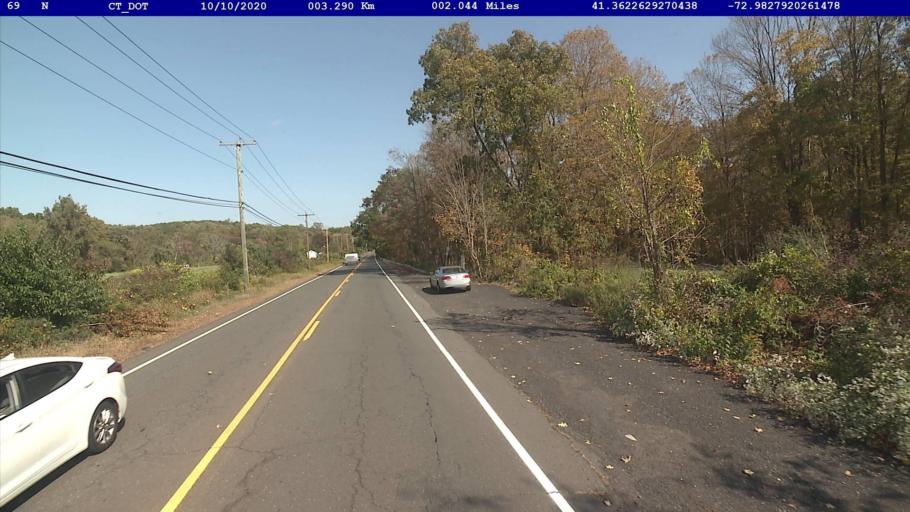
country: US
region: Connecticut
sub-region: New Haven County
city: Woodbridge
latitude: 41.3622
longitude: -72.9828
